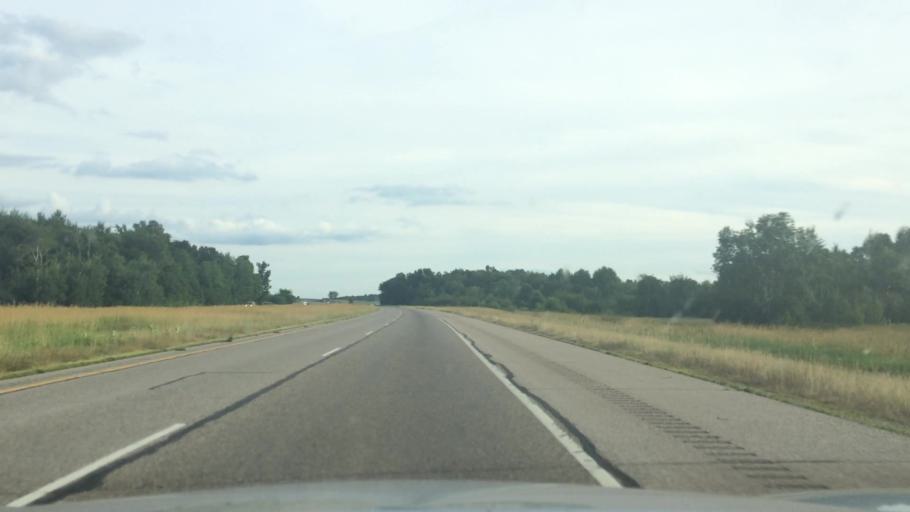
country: US
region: Wisconsin
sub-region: Waushara County
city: Wautoma
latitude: 44.1712
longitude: -89.5322
